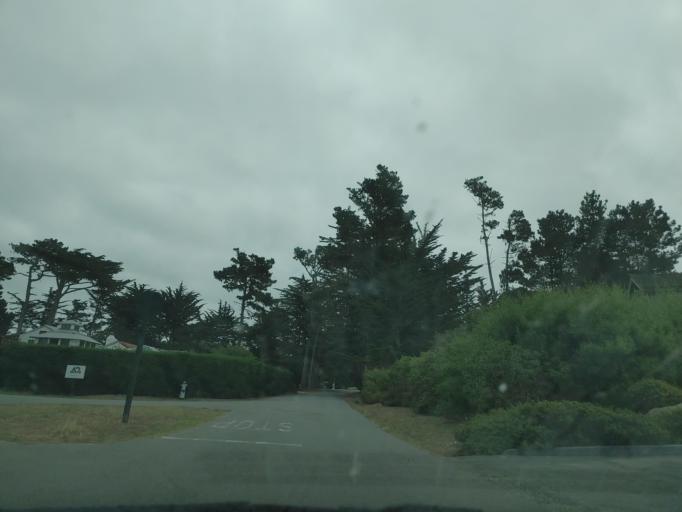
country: US
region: California
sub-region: Monterey County
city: Del Monte Forest
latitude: 36.6047
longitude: -121.9500
